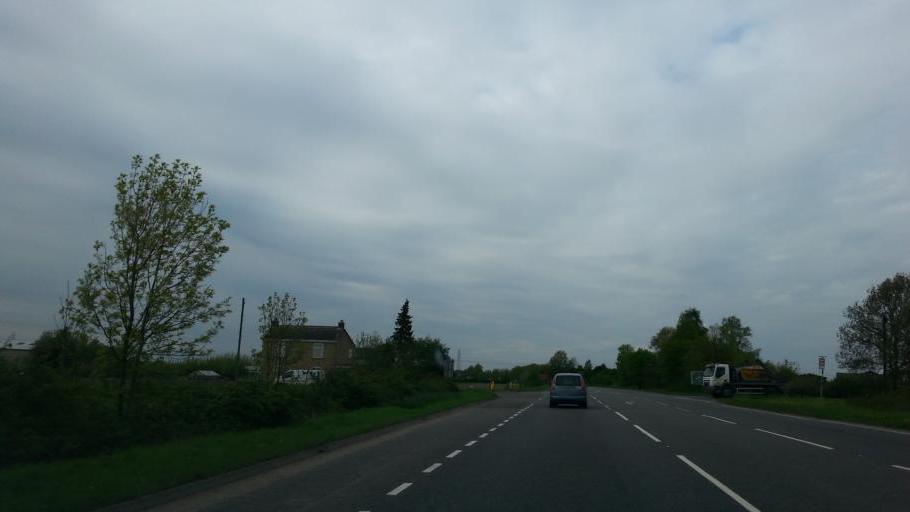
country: GB
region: England
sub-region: Cambridgeshire
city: March
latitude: 52.5442
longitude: 0.0707
